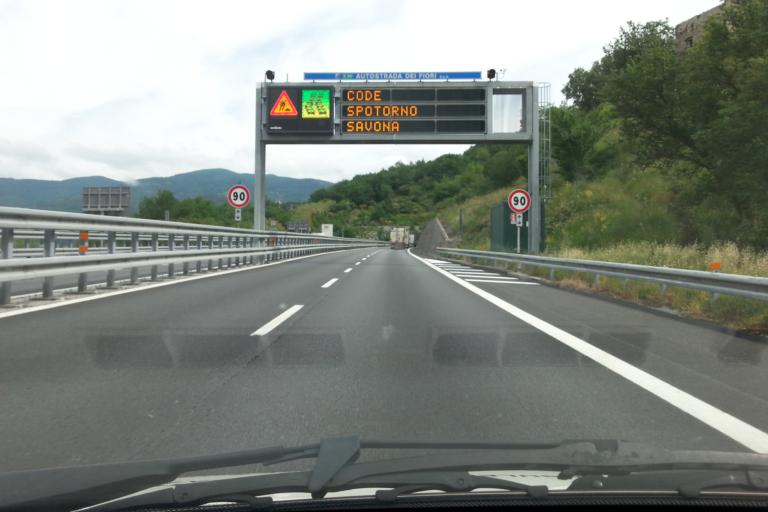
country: IT
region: Liguria
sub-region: Provincia di Savona
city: Calice Ligure
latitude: 44.1955
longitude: 8.3055
